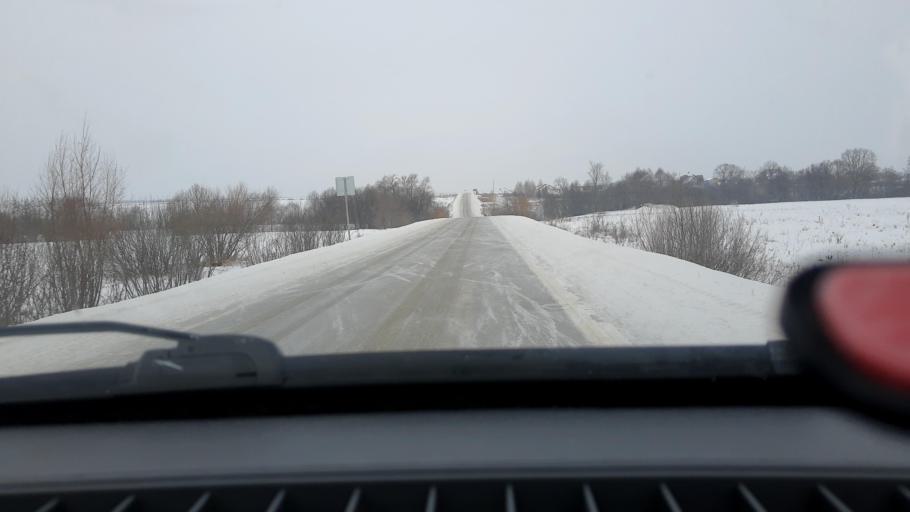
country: RU
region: Bashkortostan
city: Iglino
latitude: 54.7048
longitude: 56.4064
